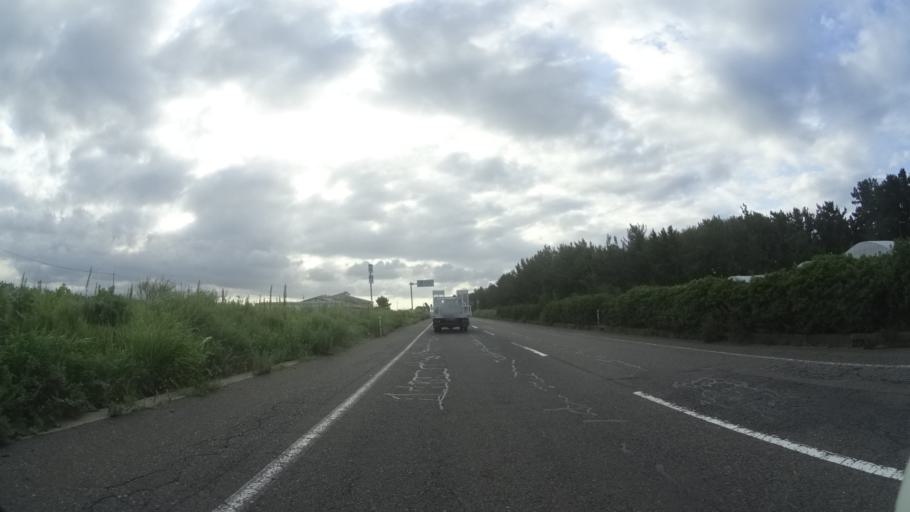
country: JP
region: Tottori
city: Kurayoshi
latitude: 35.4990
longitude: 133.7685
